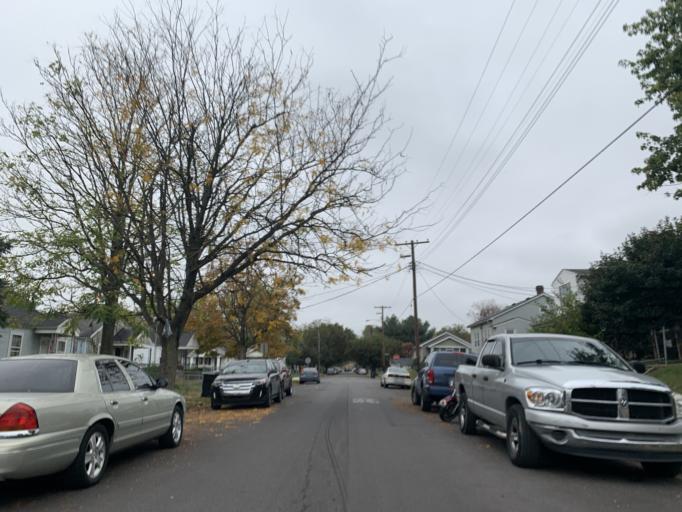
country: US
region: Indiana
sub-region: Floyd County
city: New Albany
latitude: 38.2624
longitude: -85.7964
